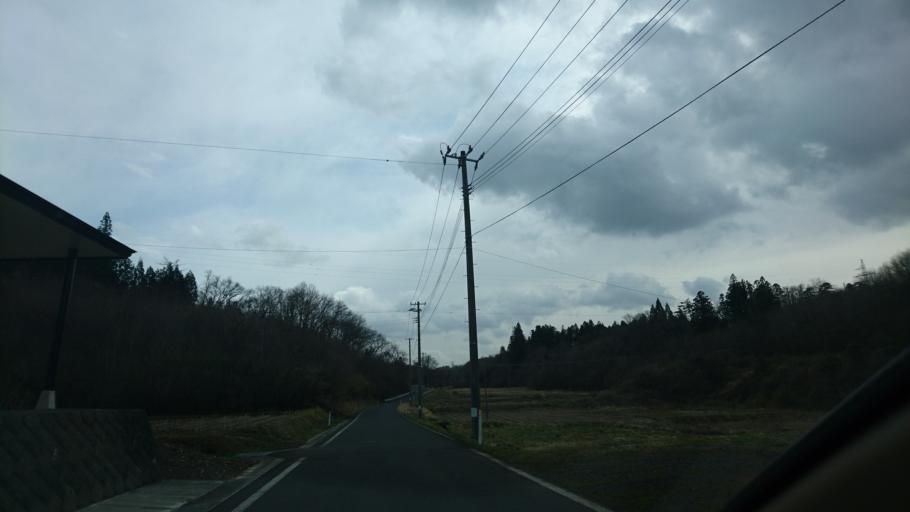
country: JP
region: Iwate
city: Ichinoseki
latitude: 38.8904
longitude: 141.1694
